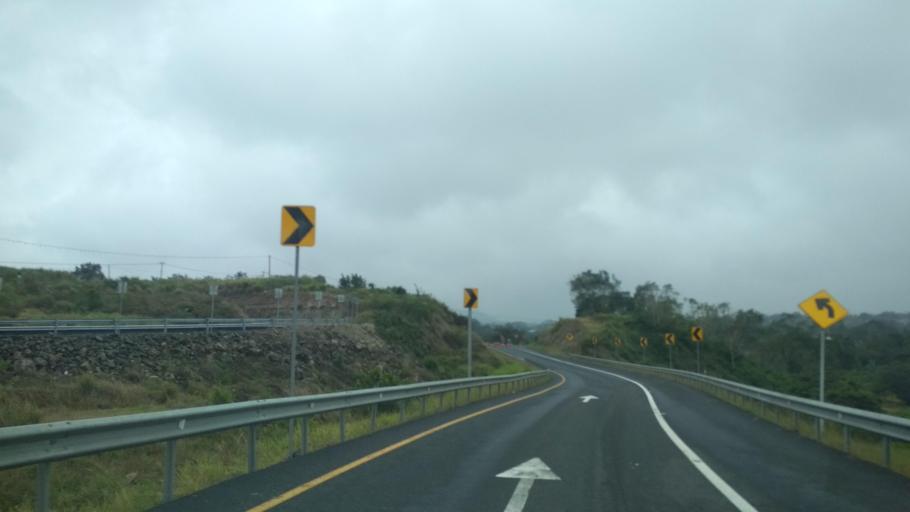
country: MX
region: Veracruz
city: Vega de San Marcos
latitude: 20.1484
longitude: -96.9479
